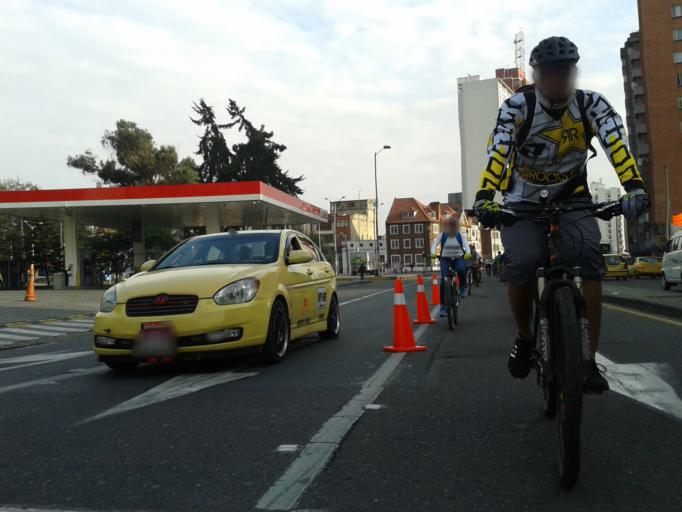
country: CO
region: Bogota D.C.
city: Bogota
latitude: 4.6440
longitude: -74.0615
